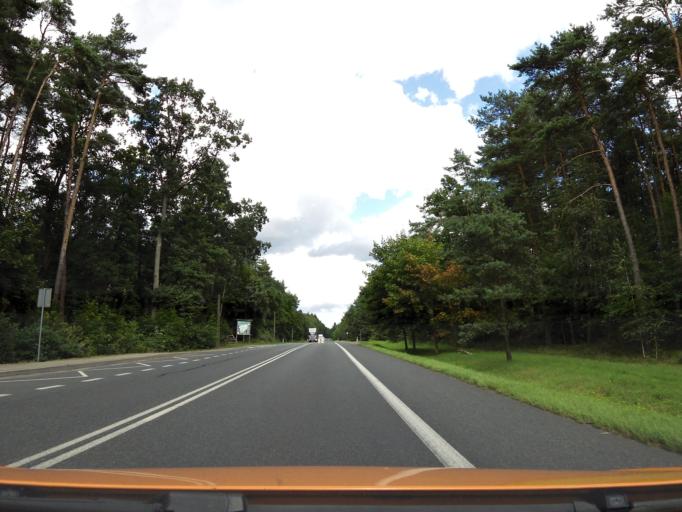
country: PL
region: West Pomeranian Voivodeship
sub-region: Powiat kolobrzeski
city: Ryman
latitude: 53.9130
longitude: 15.4490
